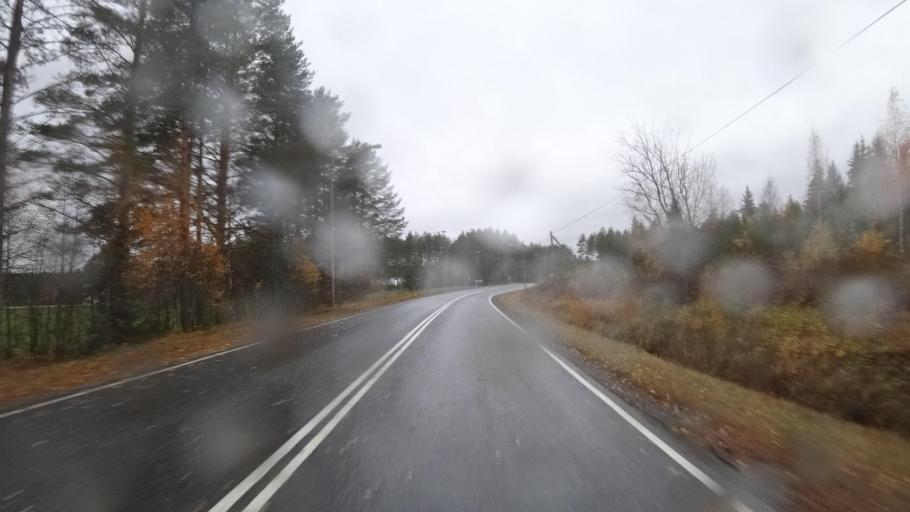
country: FI
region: Northern Savo
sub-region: Koillis-Savo
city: Tuusniemi
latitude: 62.8665
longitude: 28.3558
